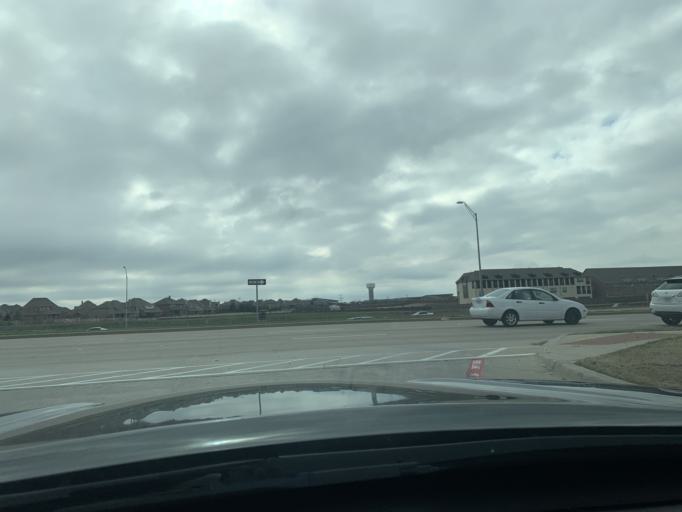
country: US
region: Texas
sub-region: Denton County
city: The Colony
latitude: 33.0563
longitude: -96.9116
